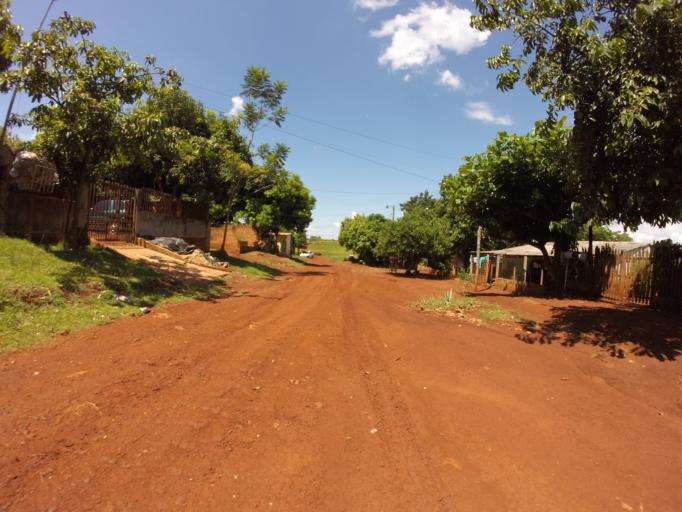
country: PY
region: Alto Parana
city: Ciudad del Este
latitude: -25.3985
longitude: -54.6350
